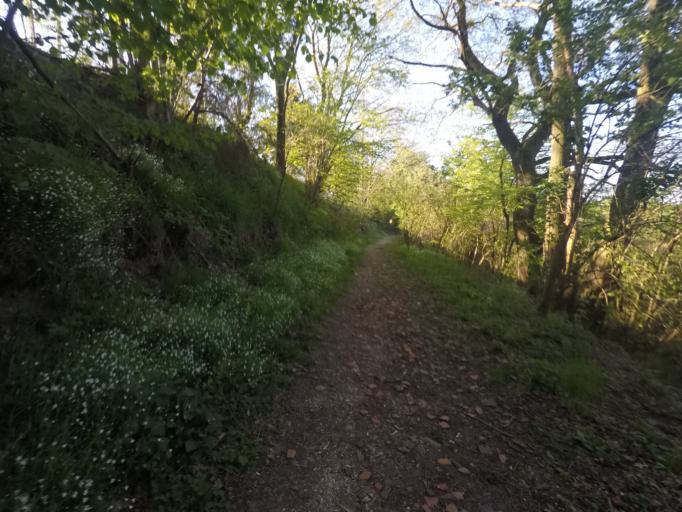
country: DE
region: North Rhine-Westphalia
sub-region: Regierungsbezirk Detmold
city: Herford
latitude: 52.0705
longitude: 8.6194
